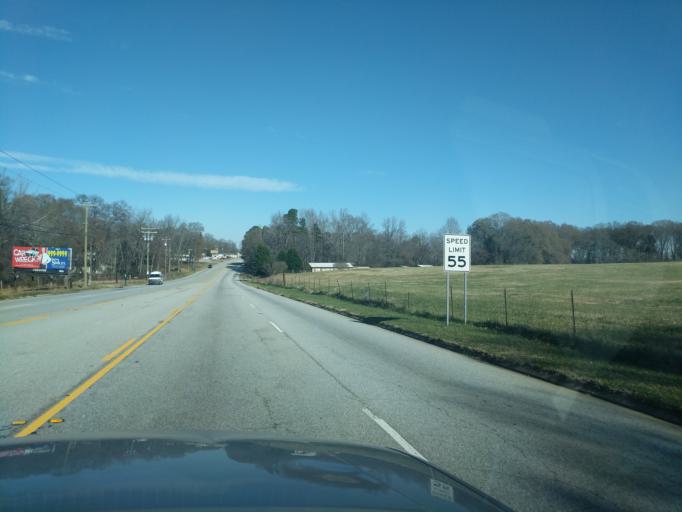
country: US
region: South Carolina
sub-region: Spartanburg County
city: Mayo
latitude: 35.0336
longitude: -81.8954
